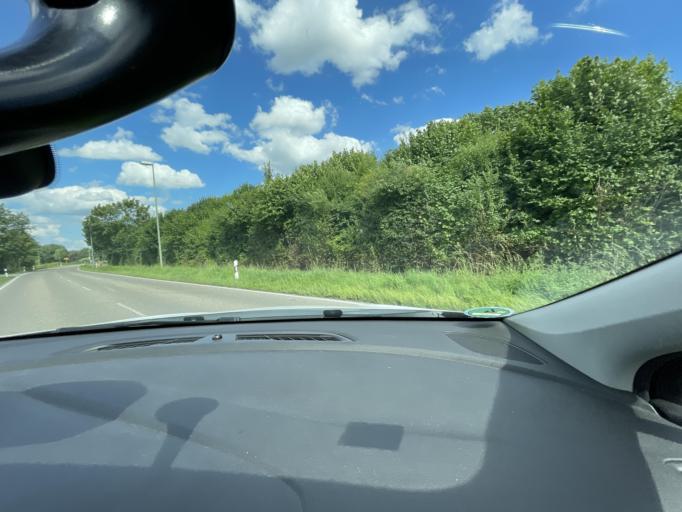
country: DE
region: Bavaria
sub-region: Swabia
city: Meitingen
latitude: 48.5545
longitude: 10.8591
